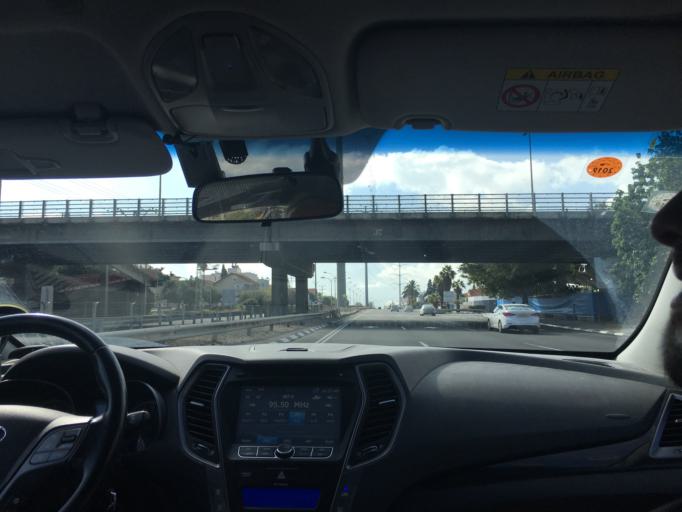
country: IL
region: Tel Aviv
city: Giv`at Shemu'el
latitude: 32.0770
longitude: 34.8441
